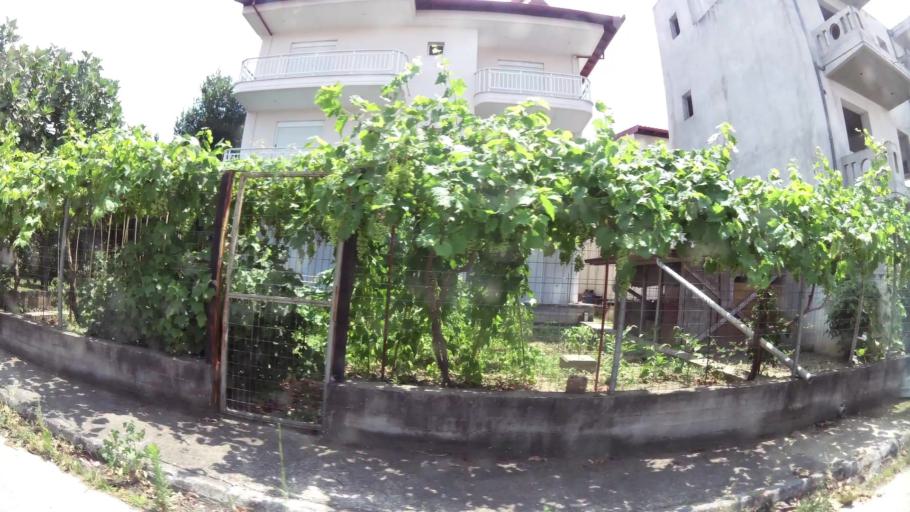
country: GR
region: Central Macedonia
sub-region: Nomos Pierias
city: Peristasi
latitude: 40.2752
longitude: 22.5378
